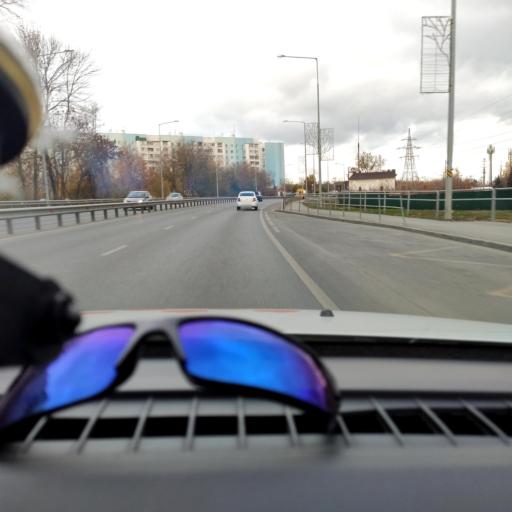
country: RU
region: Samara
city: Volzhskiy
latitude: 53.3518
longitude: 50.2156
